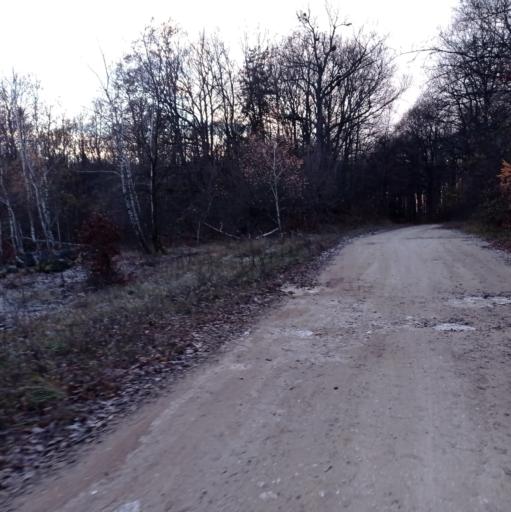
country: HU
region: Gyor-Moson-Sopron
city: Bakonyszentlaszlo
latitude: 47.3258
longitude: 17.7780
